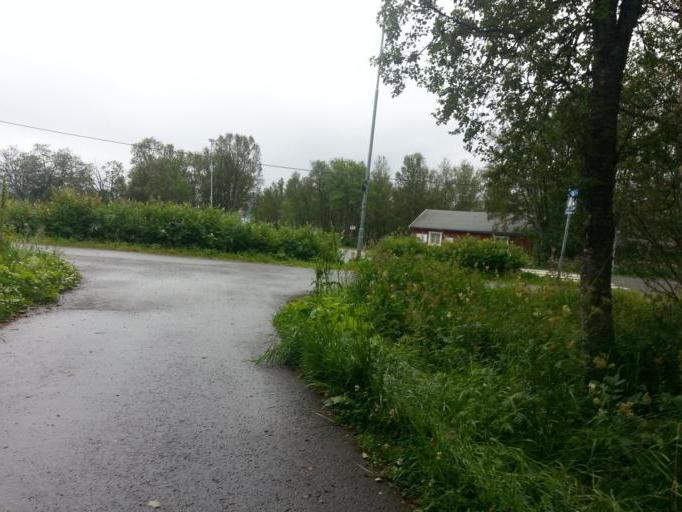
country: NO
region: Troms
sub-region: Tromso
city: Tromso
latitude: 69.6348
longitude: 18.9067
